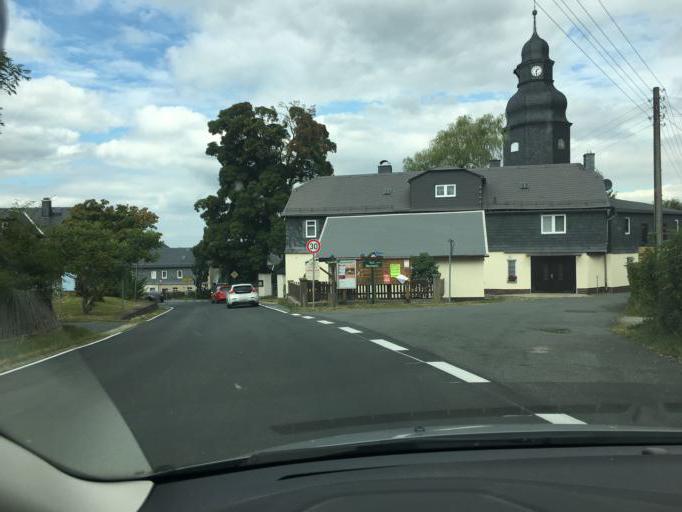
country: DE
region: Thuringia
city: Wurzbach
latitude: 50.4720
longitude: 11.5773
